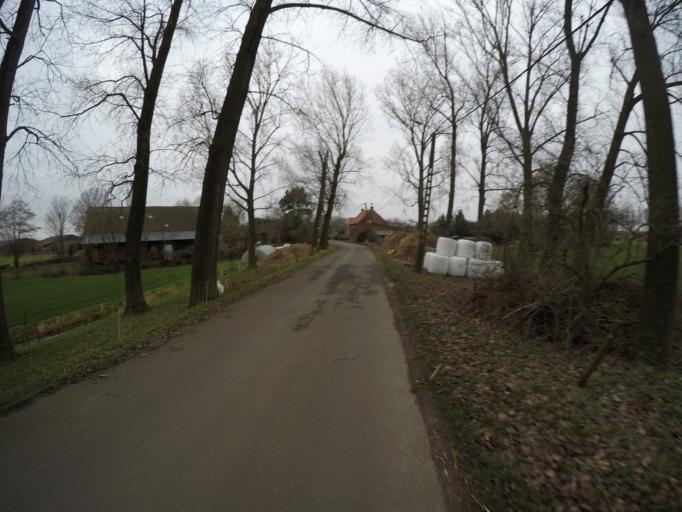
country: BE
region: Flanders
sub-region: Provincie Oost-Vlaanderen
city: Sint-Gillis-Waas
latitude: 51.2393
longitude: 4.1268
